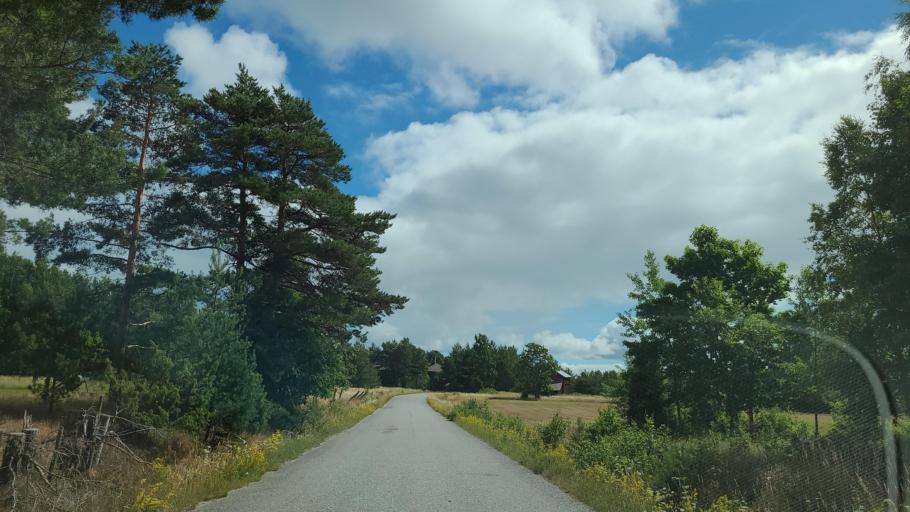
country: FI
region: Varsinais-Suomi
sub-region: Aboland-Turunmaa
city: Nagu
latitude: 60.1706
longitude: 22.0454
